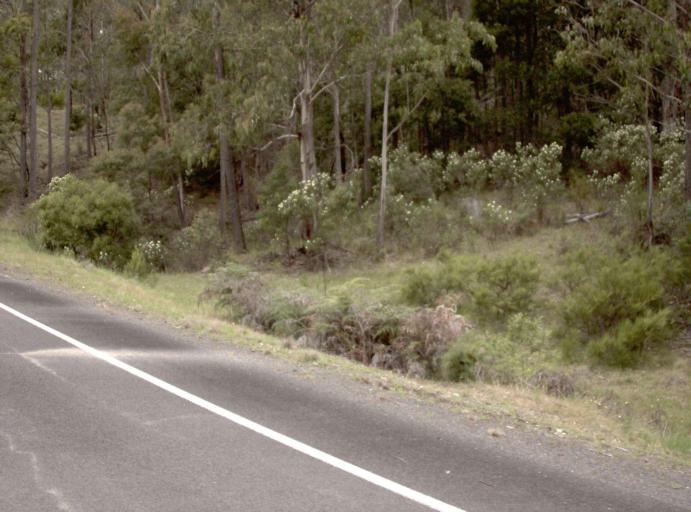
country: AU
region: New South Wales
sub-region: Bombala
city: Bombala
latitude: -37.2586
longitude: 149.2383
